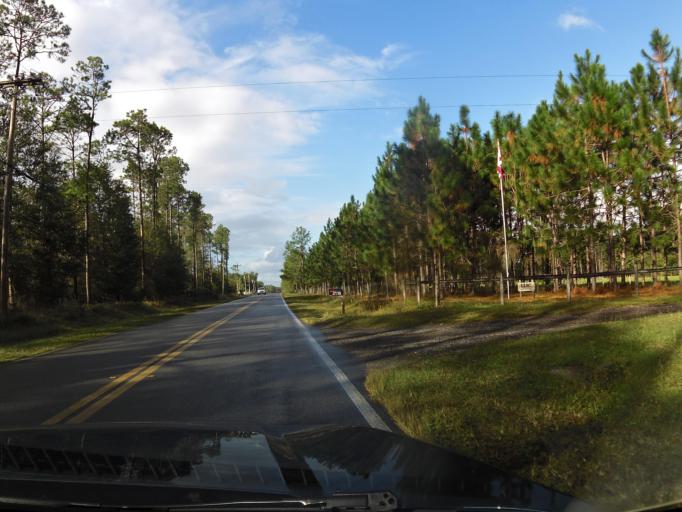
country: US
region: Florida
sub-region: Clay County
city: Asbury Lake
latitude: 30.0225
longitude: -81.8466
